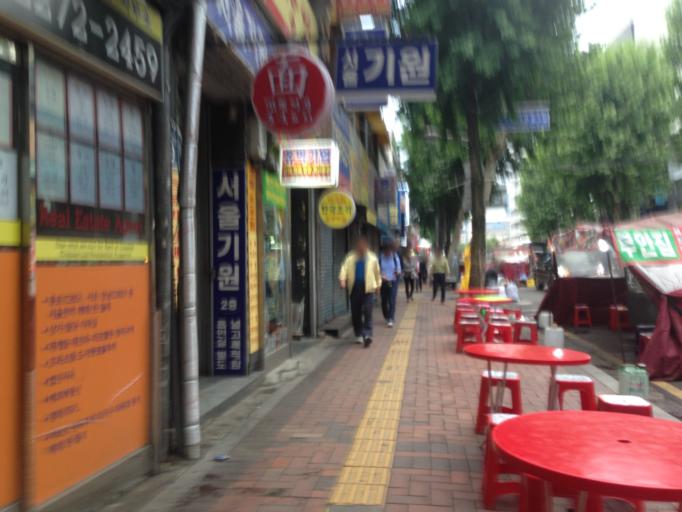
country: KR
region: Seoul
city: Seoul
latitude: 37.5696
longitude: 126.9920
